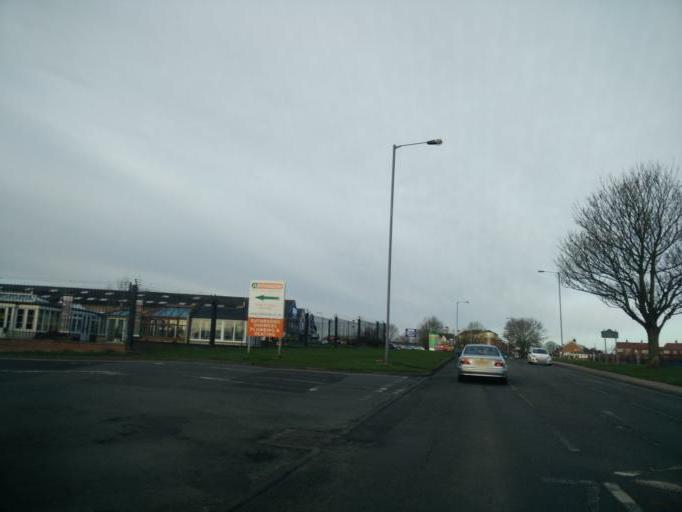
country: GB
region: England
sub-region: County Durham
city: Bishop Auckland
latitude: 54.6428
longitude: -1.6831
